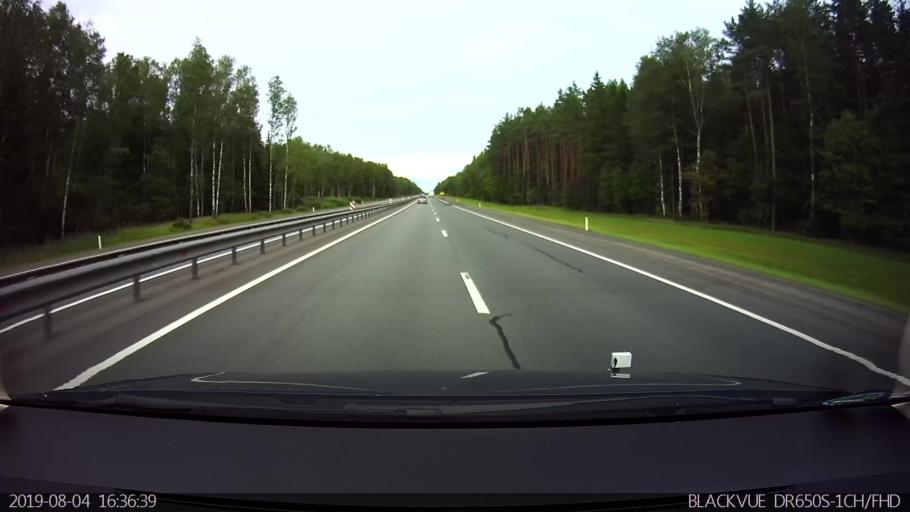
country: RU
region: Smolensk
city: Kholm-Zhirkovskiy
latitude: 55.1931
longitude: 33.8040
